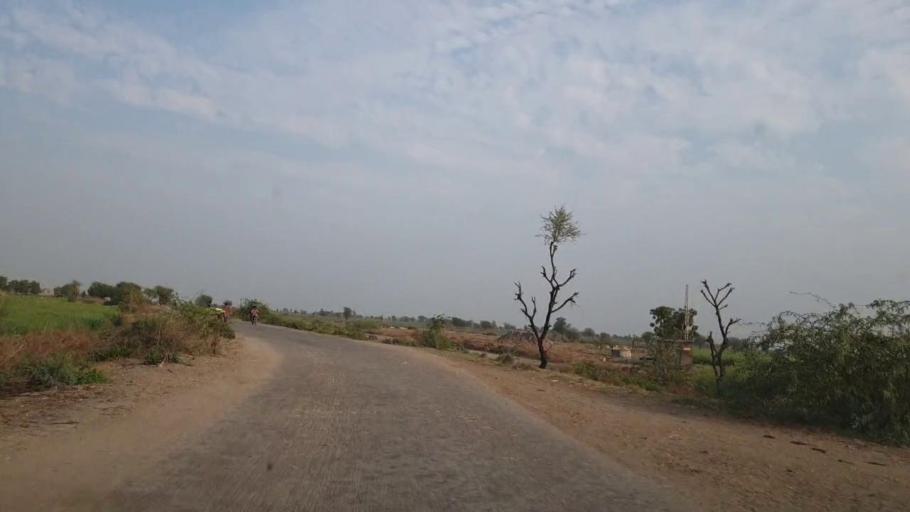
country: PK
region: Sindh
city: Mirpur Khas
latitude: 25.5572
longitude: 69.1887
